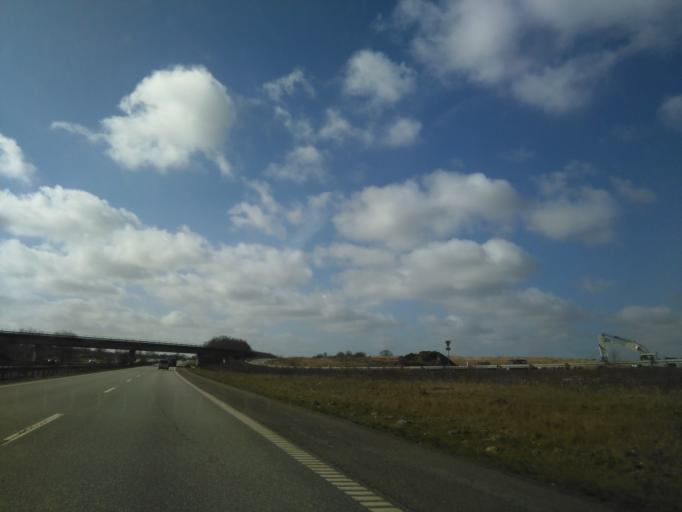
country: DK
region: Zealand
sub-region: Koge Kommune
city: Ejby
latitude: 55.4704
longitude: 12.0711
